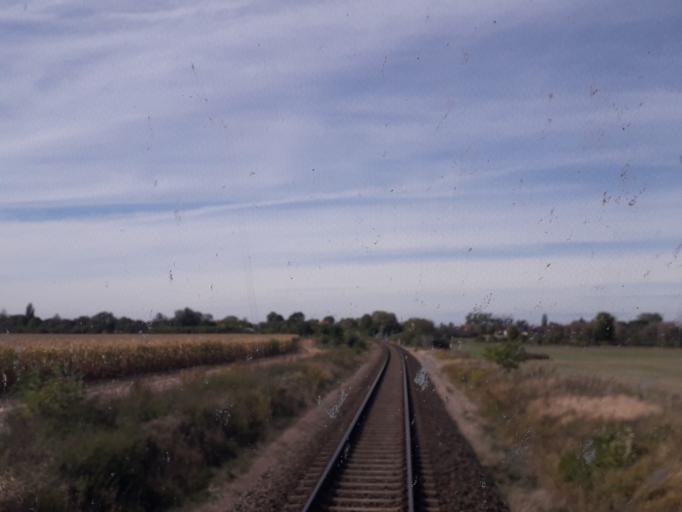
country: DE
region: Brandenburg
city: Velten
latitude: 52.7177
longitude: 13.1229
